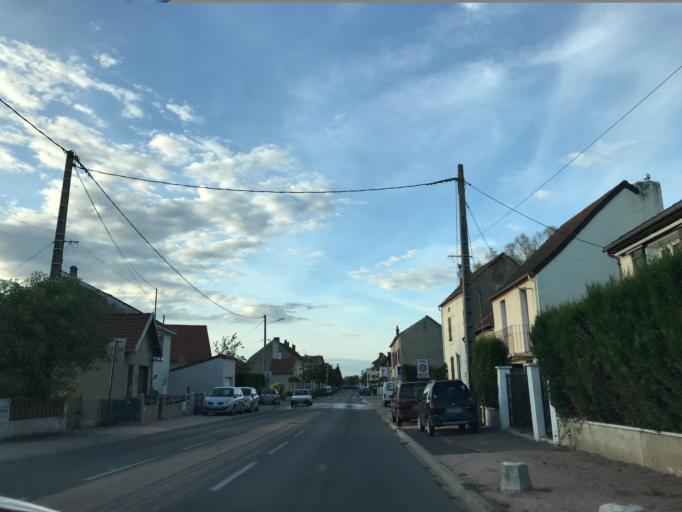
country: FR
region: Auvergne
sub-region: Departement de l'Allier
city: Abrest
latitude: 46.0961
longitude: 3.4469
